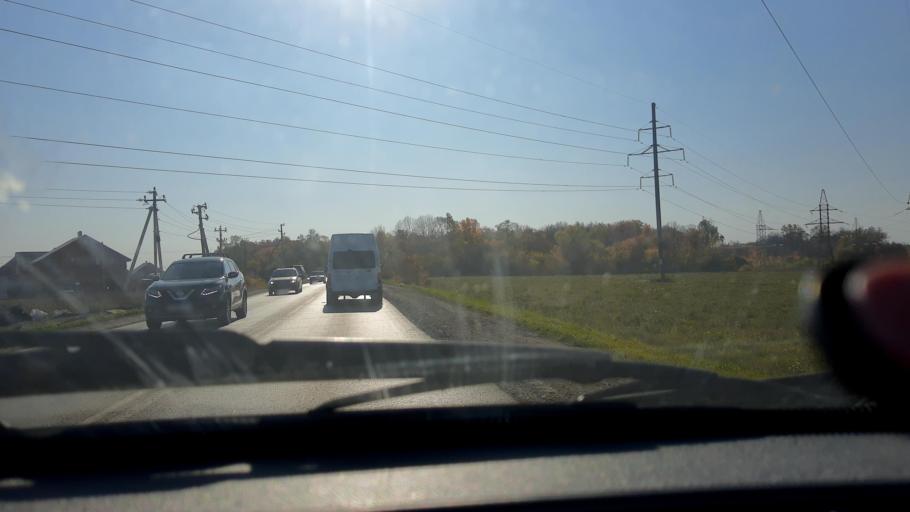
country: RU
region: Bashkortostan
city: Mikhaylovka
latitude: 54.8282
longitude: 55.8844
